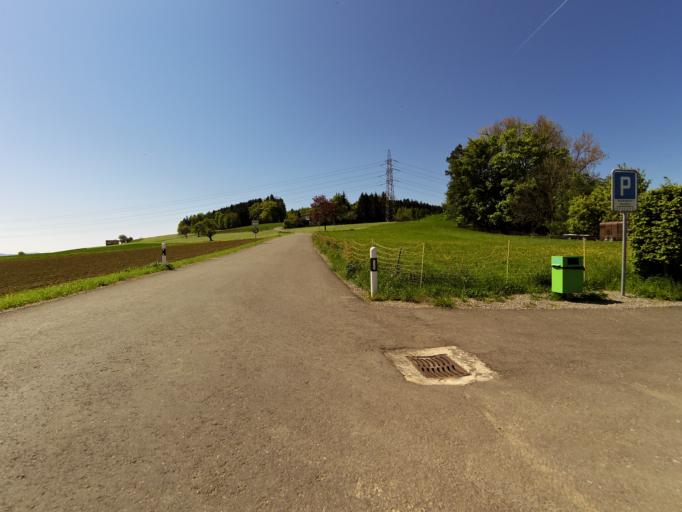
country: CH
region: Thurgau
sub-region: Weinfelden District
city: Berg
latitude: 47.5815
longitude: 9.1613
